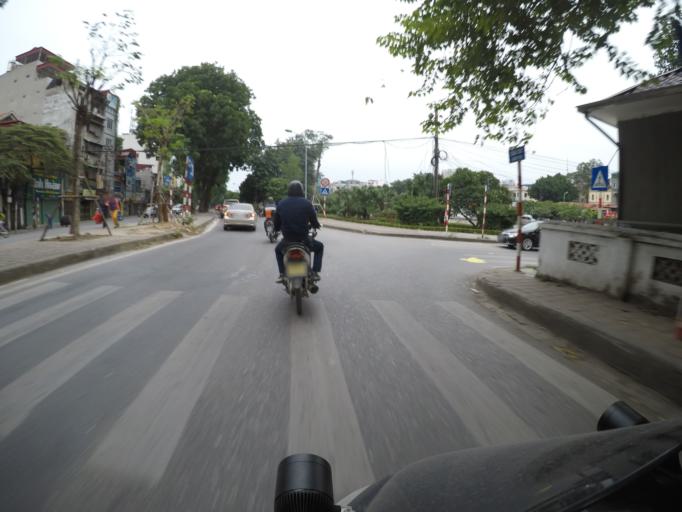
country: VN
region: Ha Noi
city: Cau Giay
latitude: 21.0242
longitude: 105.7983
